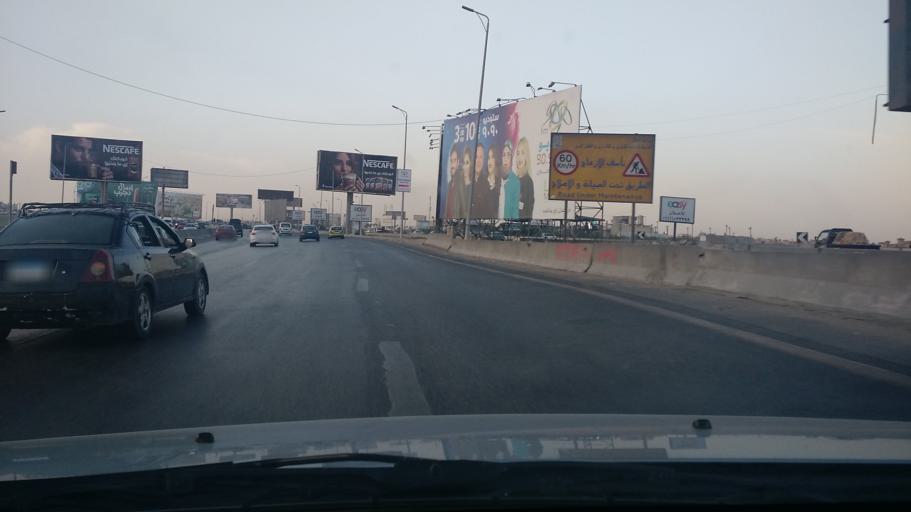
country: EG
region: Muhafazat al Qahirah
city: Cairo
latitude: 29.9819
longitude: 31.3653
